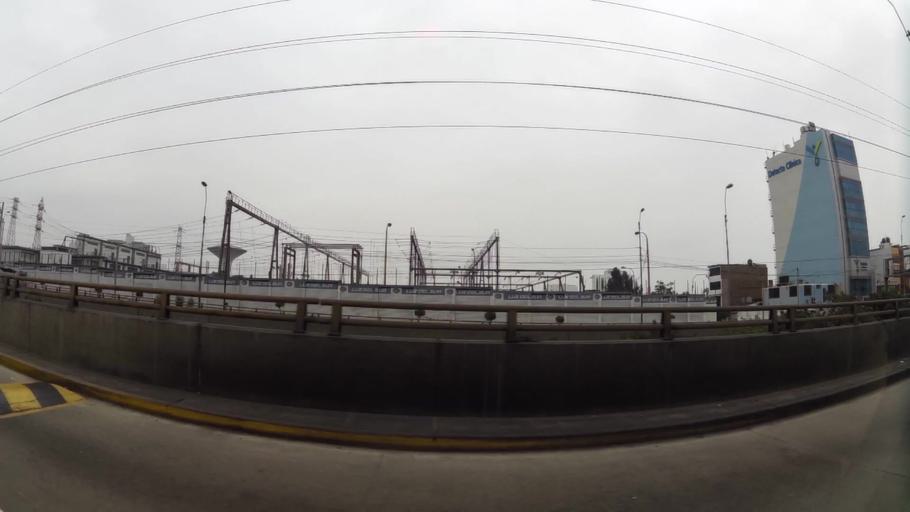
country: PE
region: Lima
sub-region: Lima
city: Surco
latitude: -12.1112
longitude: -76.9952
